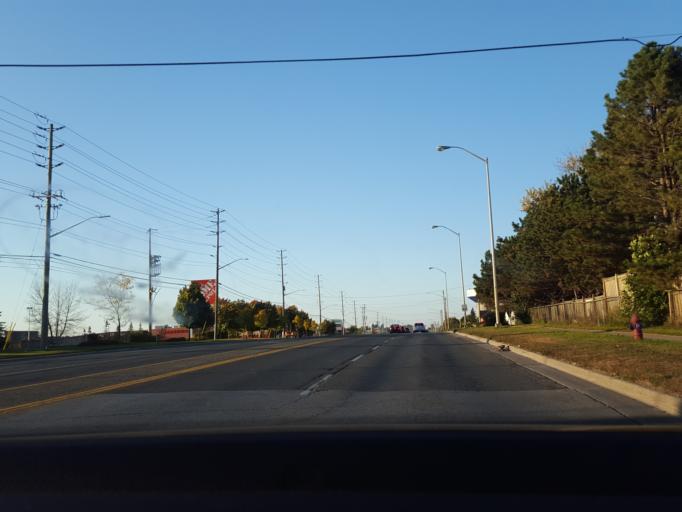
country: CA
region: Ontario
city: Newmarket
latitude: 44.0613
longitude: -79.4818
